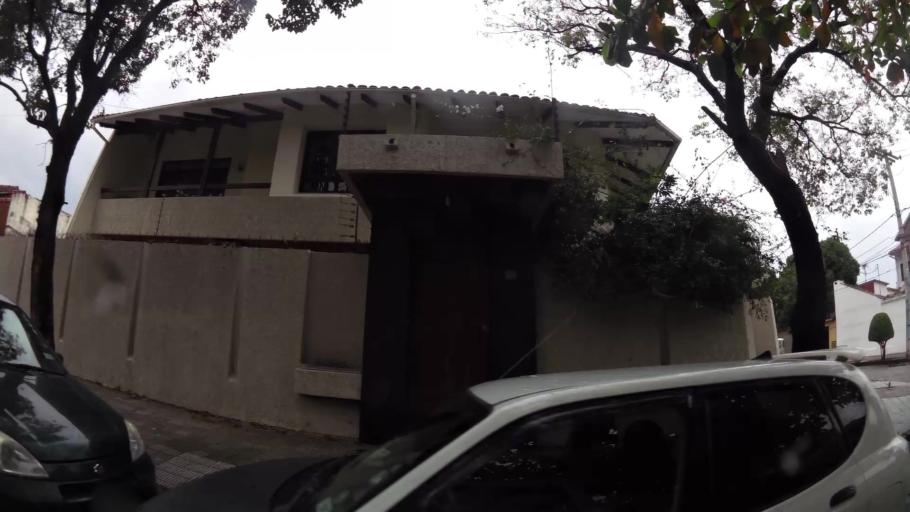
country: BO
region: Santa Cruz
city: Santa Cruz de la Sierra
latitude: -17.7968
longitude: -63.1735
